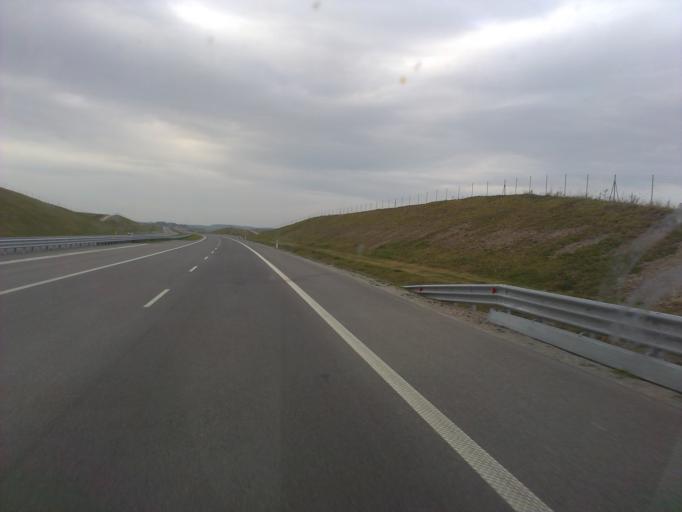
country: PL
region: Subcarpathian Voivodeship
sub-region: Powiat jaroslawski
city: Rokietnica
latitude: 49.9312
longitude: 22.7134
